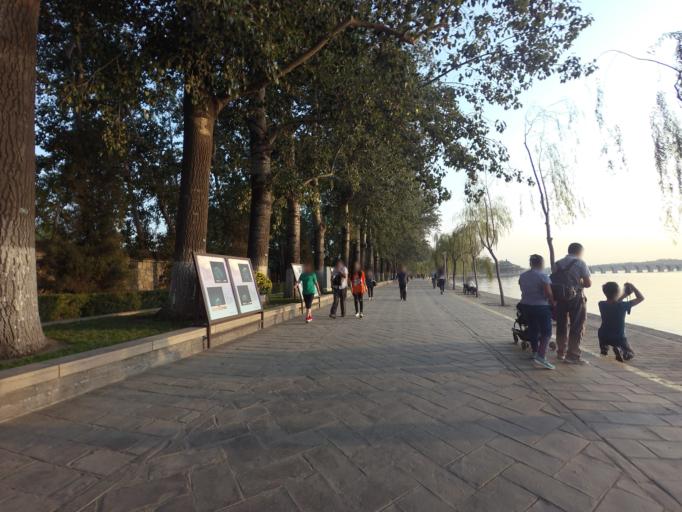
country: CN
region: Beijing
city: Haidian
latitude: 39.9923
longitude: 116.2744
